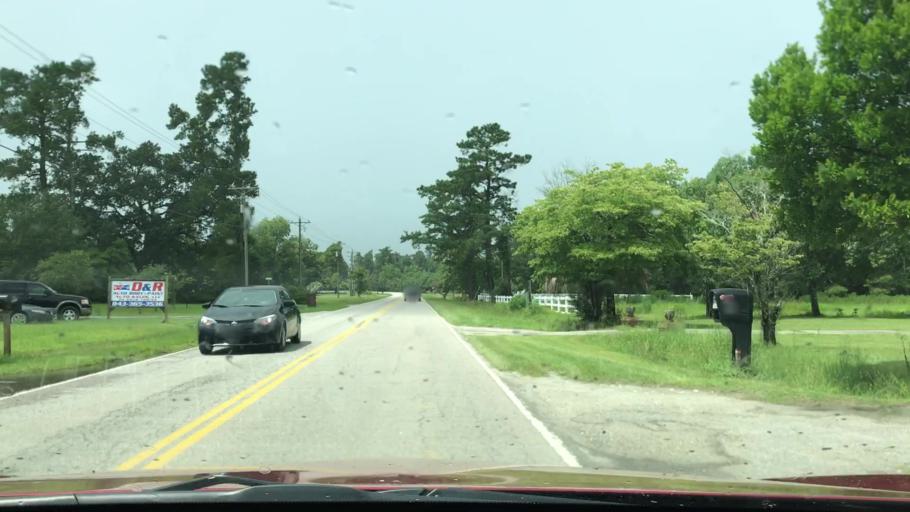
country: US
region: South Carolina
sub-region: Horry County
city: Red Hill
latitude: 33.8881
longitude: -78.9565
